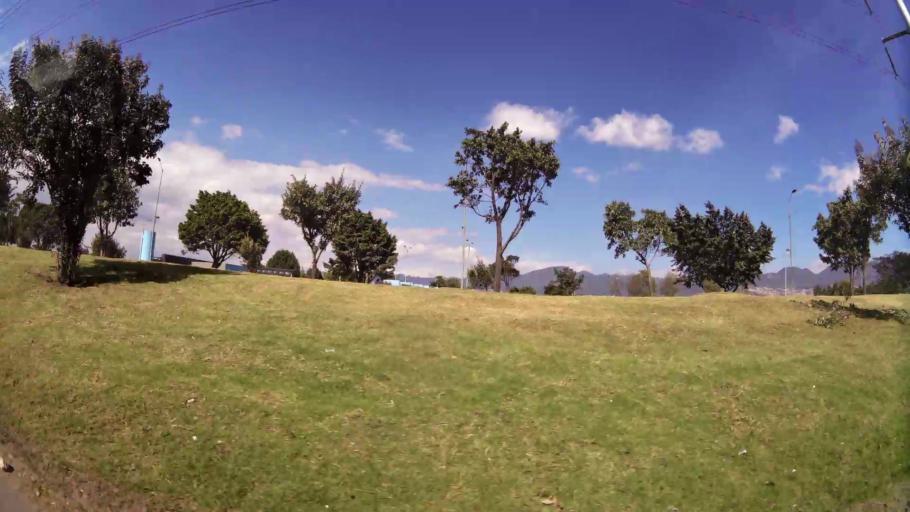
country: CO
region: Bogota D.C.
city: Bogota
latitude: 4.5703
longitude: -74.1390
